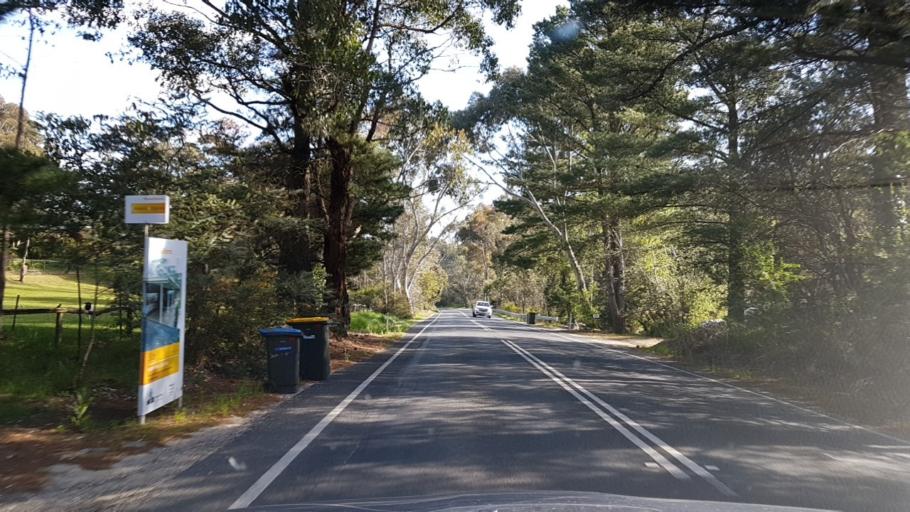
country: AU
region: South Australia
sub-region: Adelaide Hills
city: Lobethal
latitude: -34.8797
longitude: 138.8910
